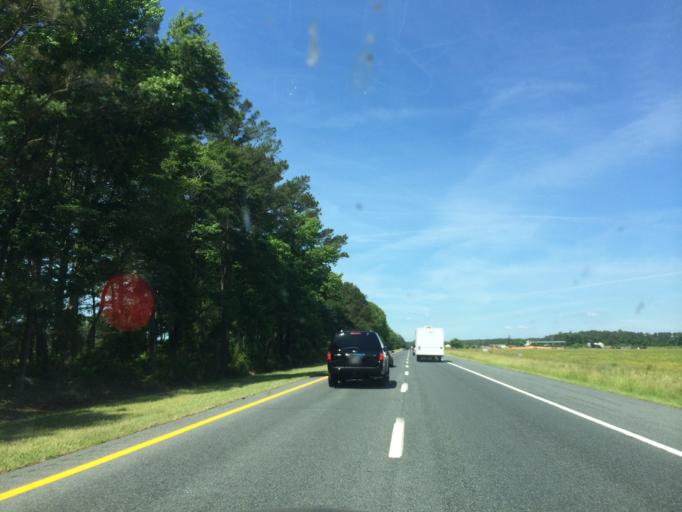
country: US
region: Maryland
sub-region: Wicomico County
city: Pittsville
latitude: 38.3834
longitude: -75.4447
